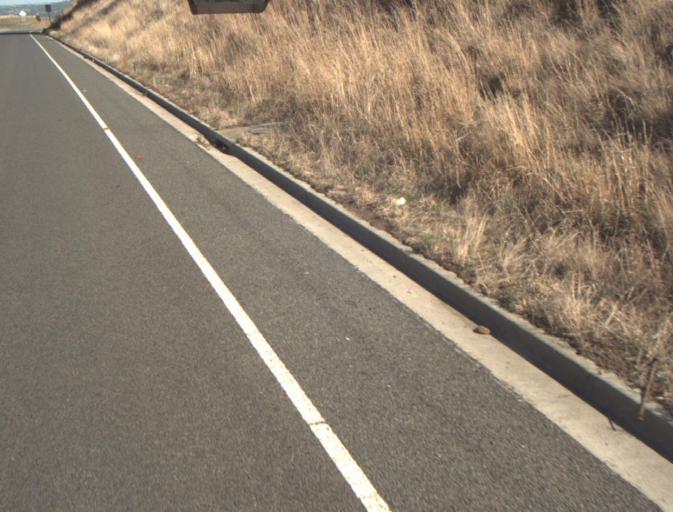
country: AU
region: Tasmania
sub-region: Launceston
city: Mayfield
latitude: -41.3703
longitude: 147.1096
